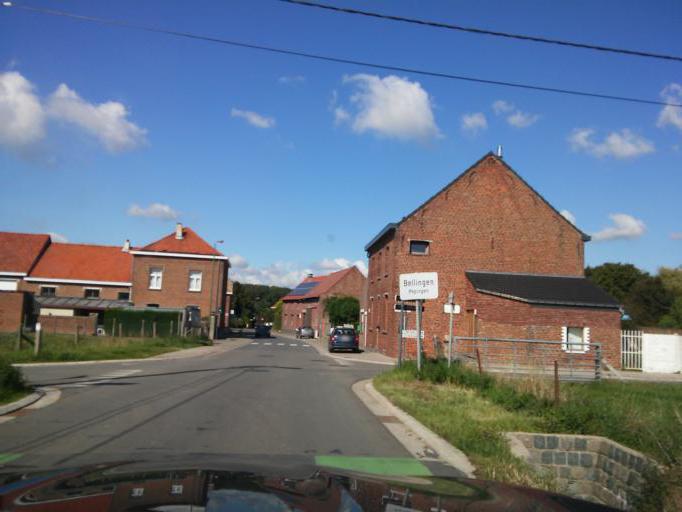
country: BE
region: Flanders
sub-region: Provincie Vlaams-Brabant
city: Pepingen
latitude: 50.7397
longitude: 4.1555
